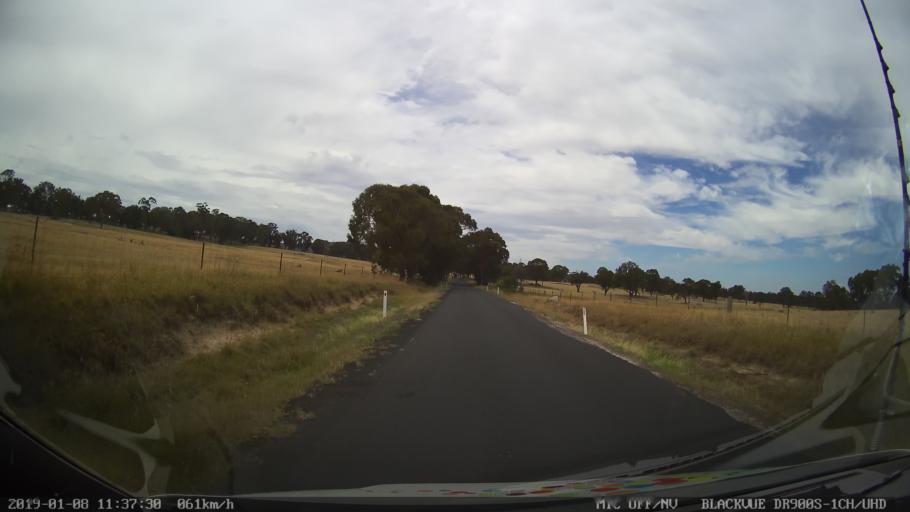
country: AU
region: New South Wales
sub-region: Guyra
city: Guyra
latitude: -30.3526
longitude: 151.5522
